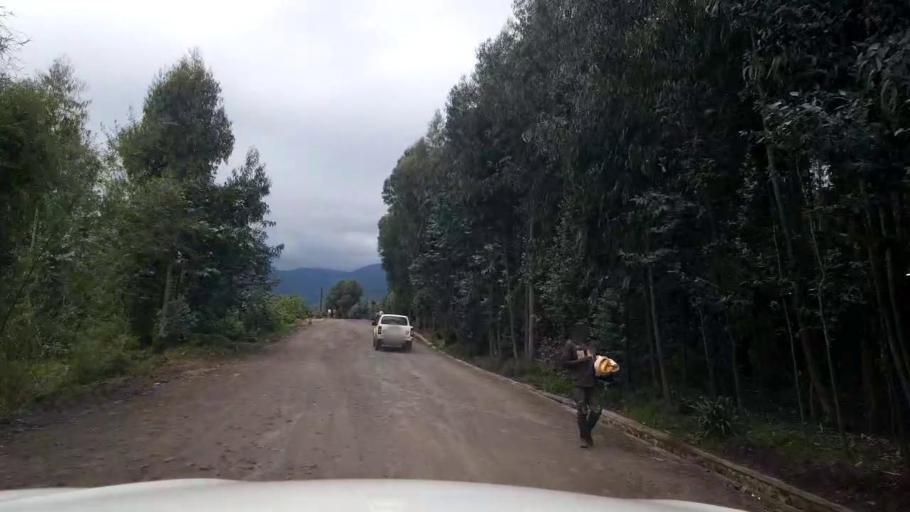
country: RW
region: Northern Province
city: Musanze
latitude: -1.4454
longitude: 29.5314
